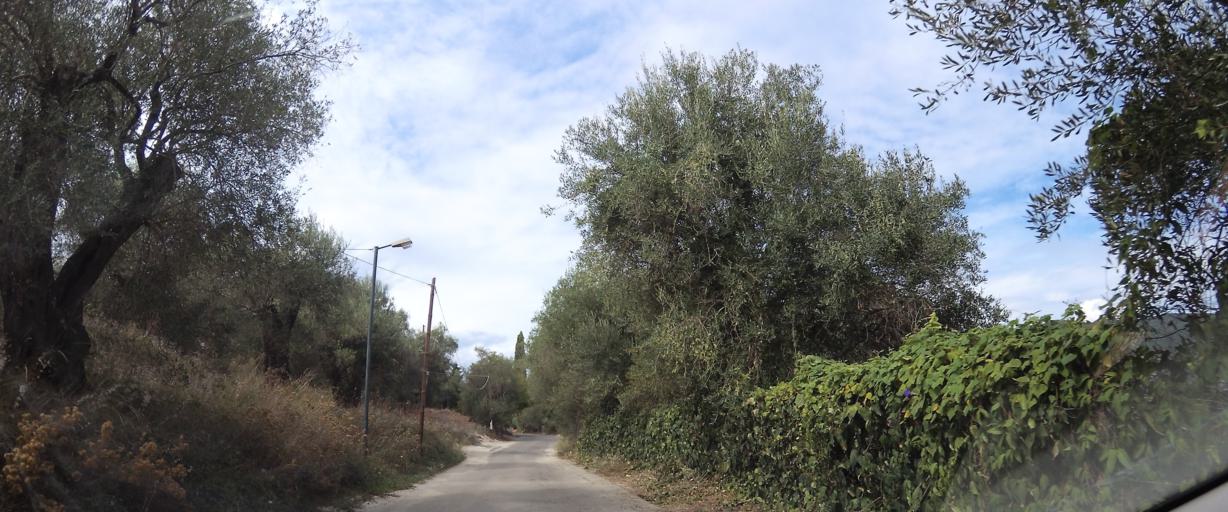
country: GR
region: Ionian Islands
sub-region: Nomos Kerkyras
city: Kontokali
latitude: 39.6918
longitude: 19.8147
